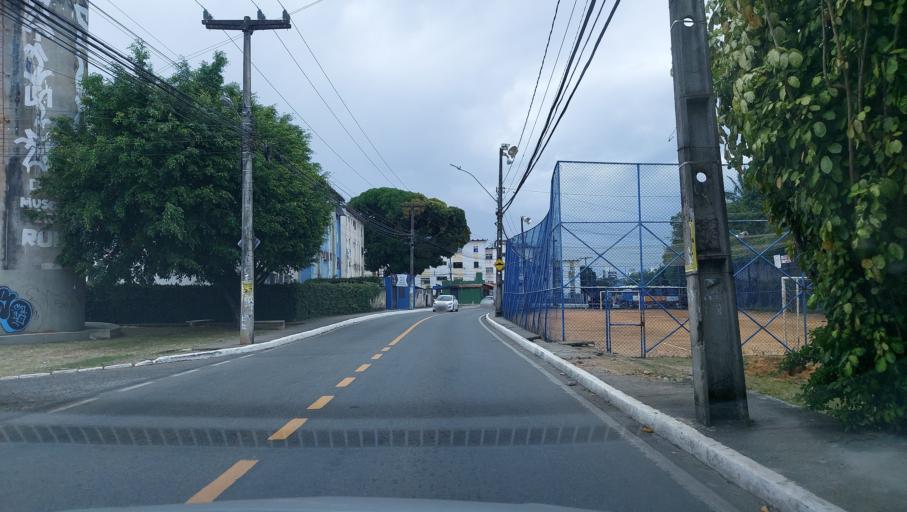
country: BR
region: Bahia
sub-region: Salvador
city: Salvador
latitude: -12.9646
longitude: -38.4434
